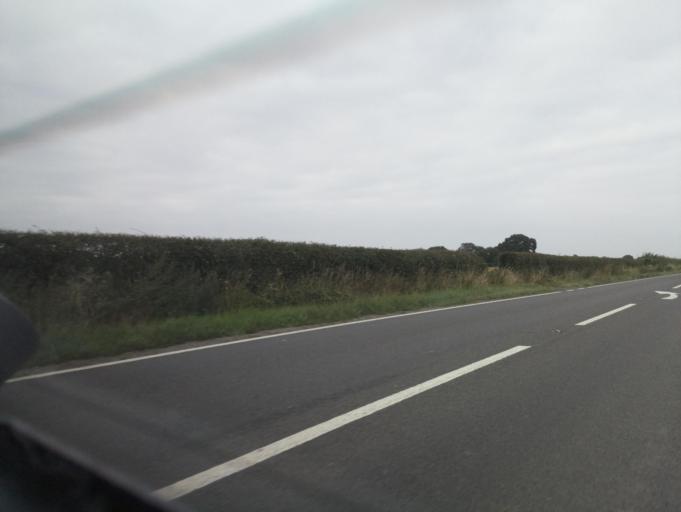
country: GB
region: England
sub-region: Shropshire
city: Shawbury
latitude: 52.7732
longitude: -2.6711
